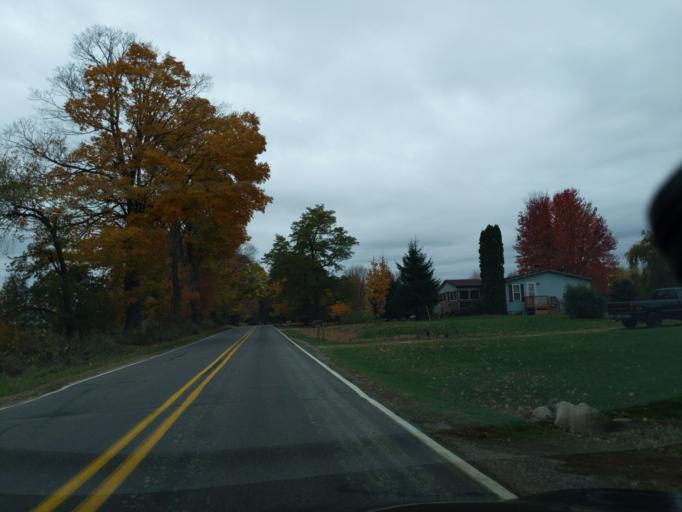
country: US
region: Michigan
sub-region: Jackson County
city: Spring Arbor
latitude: 42.3238
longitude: -84.6004
